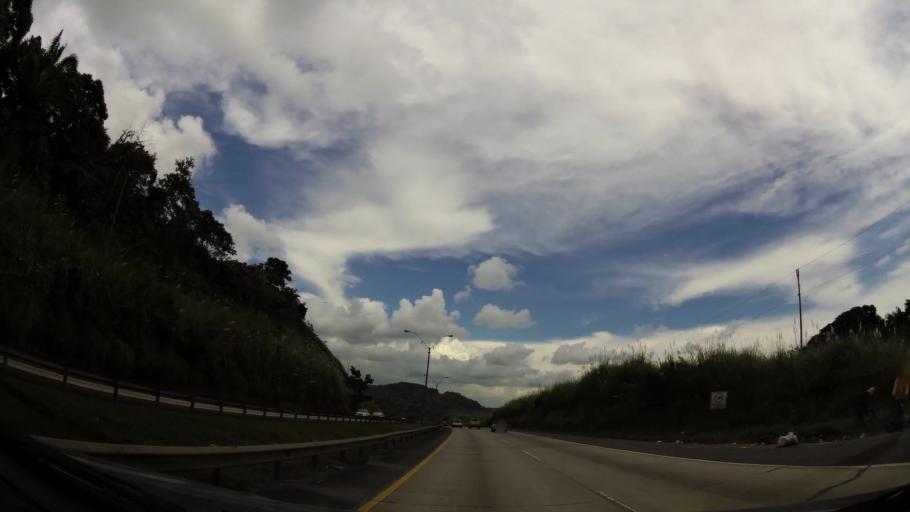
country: PA
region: Panama
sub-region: Distrito Arraijan
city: Arraijan
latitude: 8.9654
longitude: -79.6472
